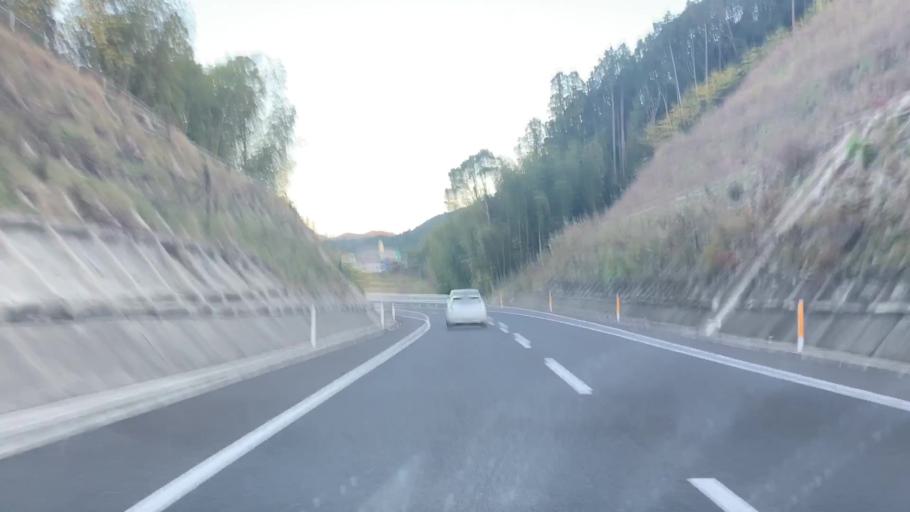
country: JP
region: Saga Prefecture
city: Takeocho-takeo
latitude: 33.2556
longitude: 129.9823
